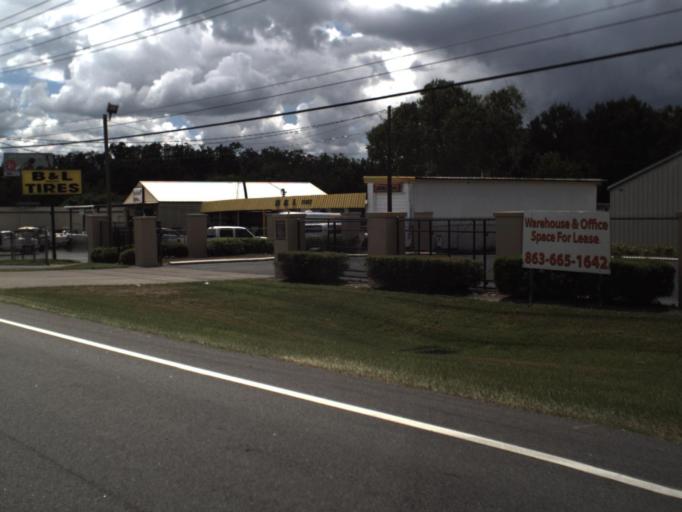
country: US
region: Florida
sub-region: Polk County
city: Crystal Lake
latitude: 28.0040
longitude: -81.9044
